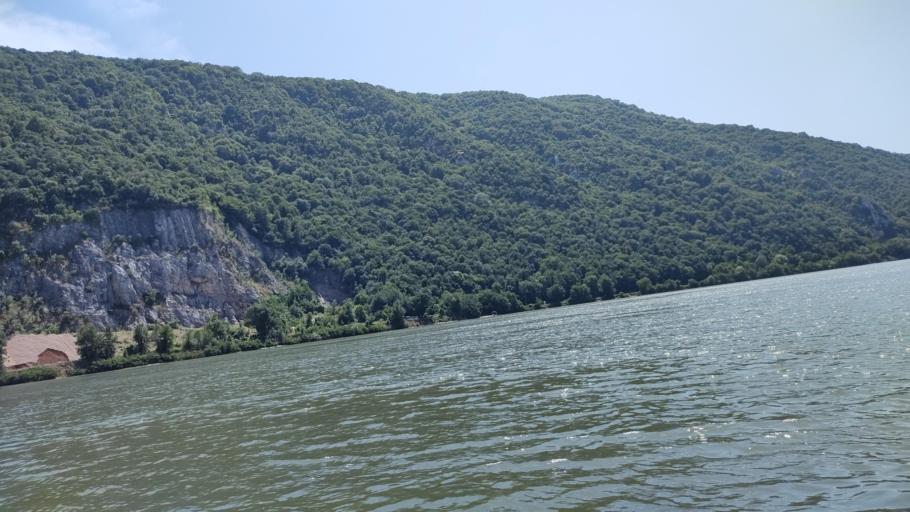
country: RO
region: Caras-Severin
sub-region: Comuna Pescari
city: Coronini
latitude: 44.6544
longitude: 21.7282
